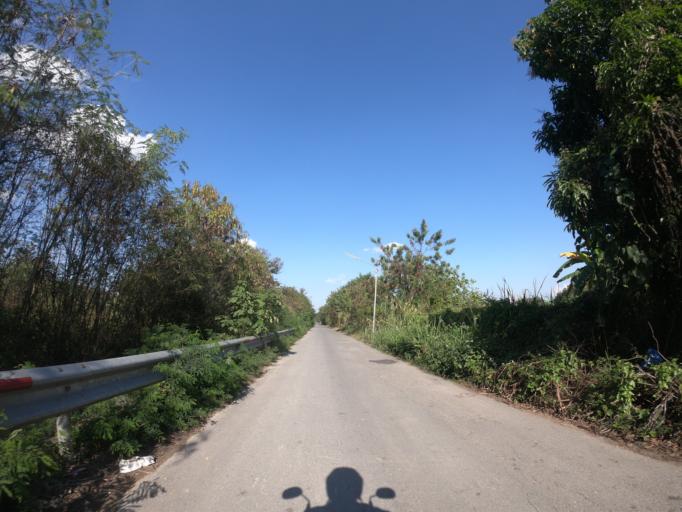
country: TH
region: Chiang Mai
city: Chiang Mai
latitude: 18.7497
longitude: 98.9652
